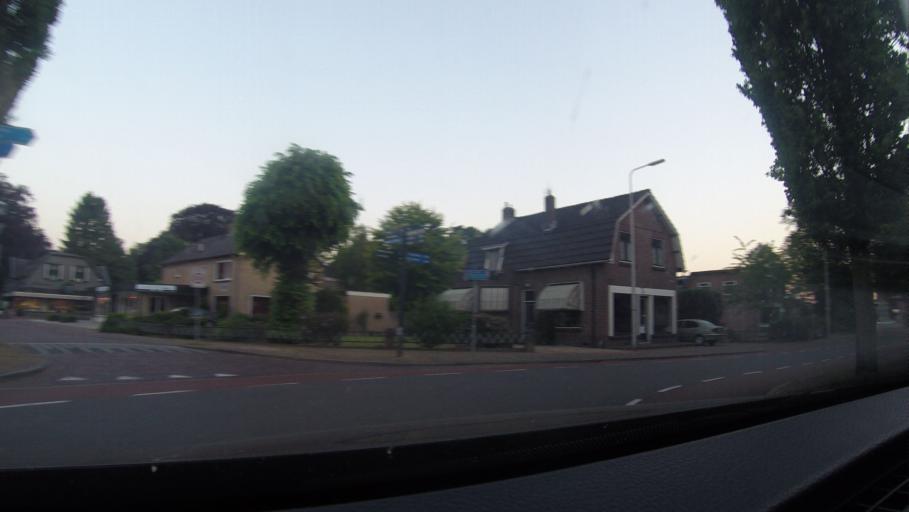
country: NL
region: Gelderland
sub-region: Gemeente Lochem
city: Harfsen
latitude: 52.2513
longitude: 6.2879
